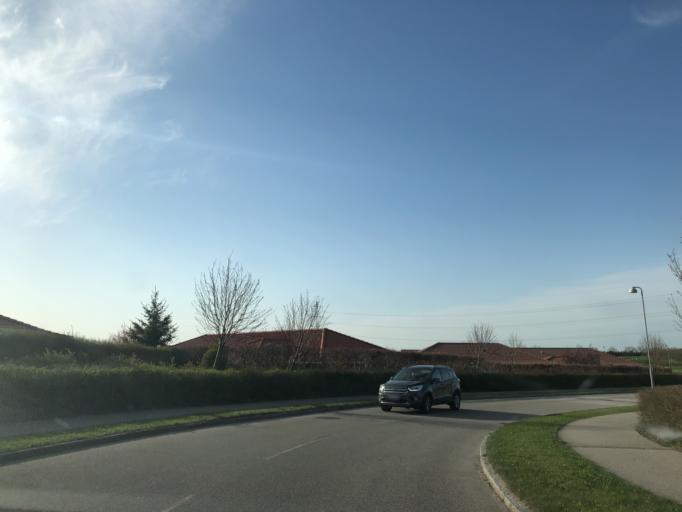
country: DK
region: Zealand
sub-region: Ringsted Kommune
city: Ringsted
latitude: 55.4522
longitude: 11.7793
